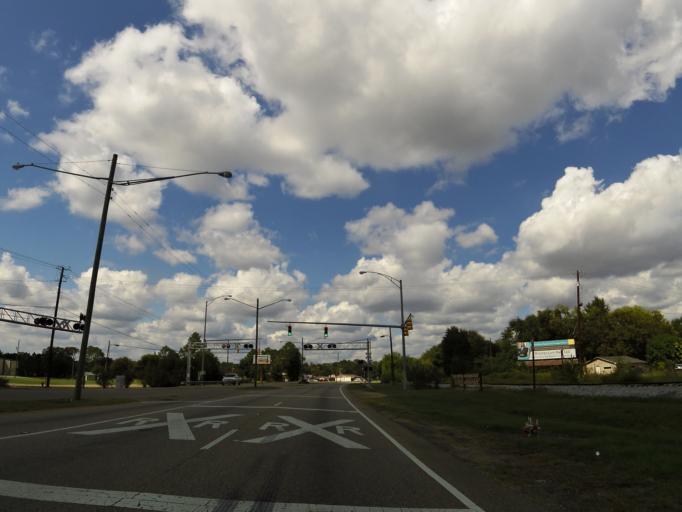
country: US
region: Alabama
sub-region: Dallas County
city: Selmont-West Selmont
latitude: 32.3714
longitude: -87.0065
